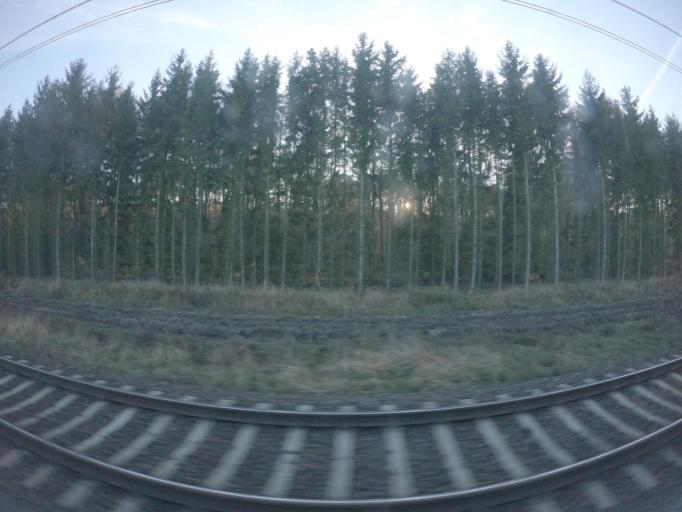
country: PL
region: Lubusz
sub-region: Powiat slubicki
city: Rzepin
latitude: 52.2698
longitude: 14.9274
